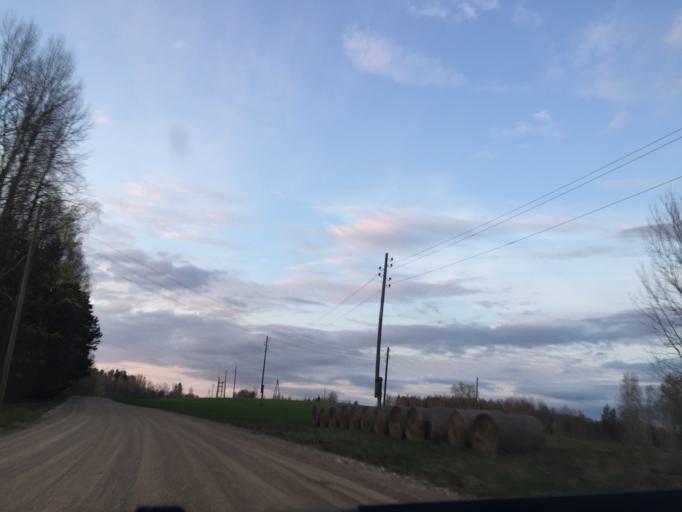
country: LV
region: Aluksnes Rajons
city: Aluksne
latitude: 57.3238
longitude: 26.9413
